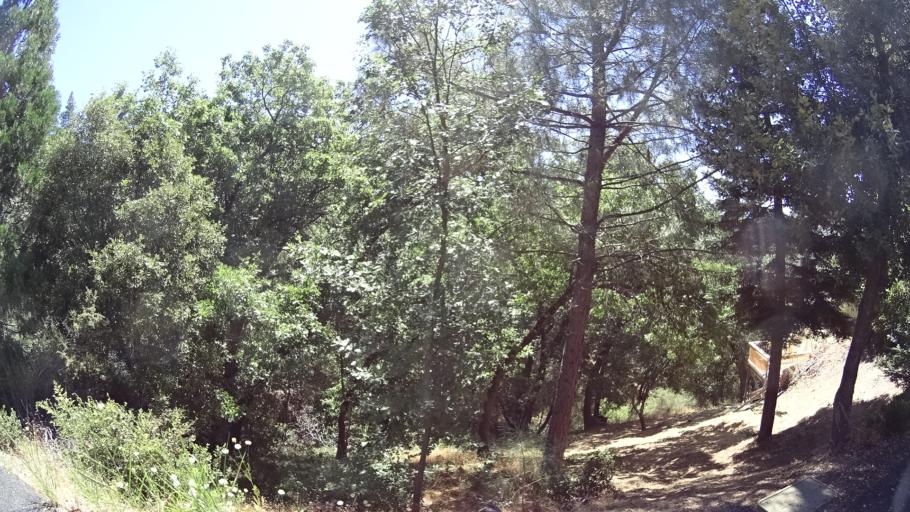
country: US
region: California
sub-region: Calaveras County
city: Forest Meadows
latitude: 38.1870
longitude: -120.3645
